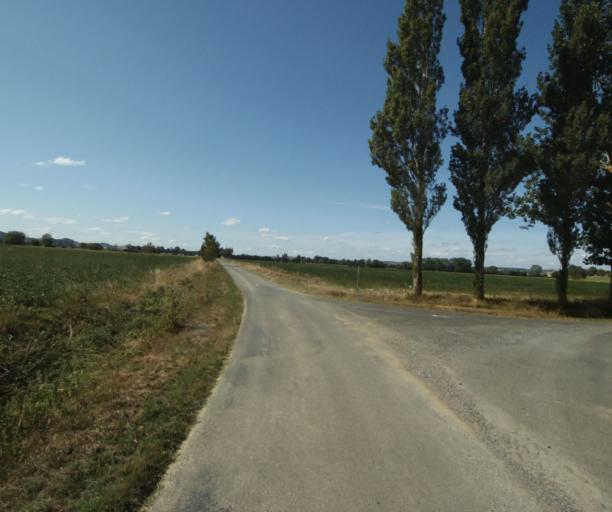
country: FR
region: Midi-Pyrenees
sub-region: Departement de la Haute-Garonne
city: Revel
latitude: 43.4904
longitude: 1.9907
